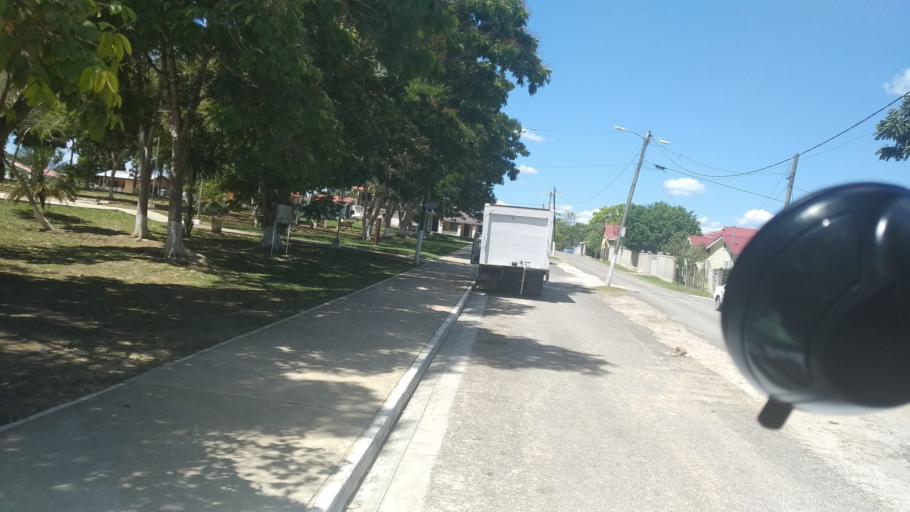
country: BZ
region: Cayo
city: Benque Viejo del Carmen
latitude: 17.0729
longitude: -89.1408
